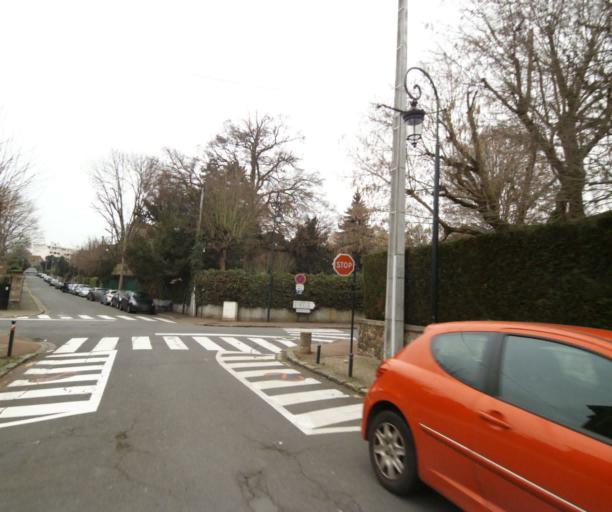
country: FR
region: Ile-de-France
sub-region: Departement des Hauts-de-Seine
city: Garches
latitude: 48.8423
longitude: 2.1875
